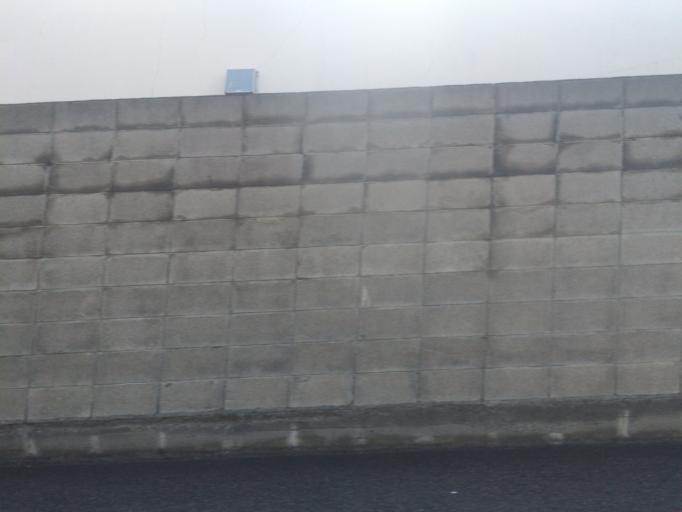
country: JP
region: Hokkaido
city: Sapporo
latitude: 43.0322
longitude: 141.3519
